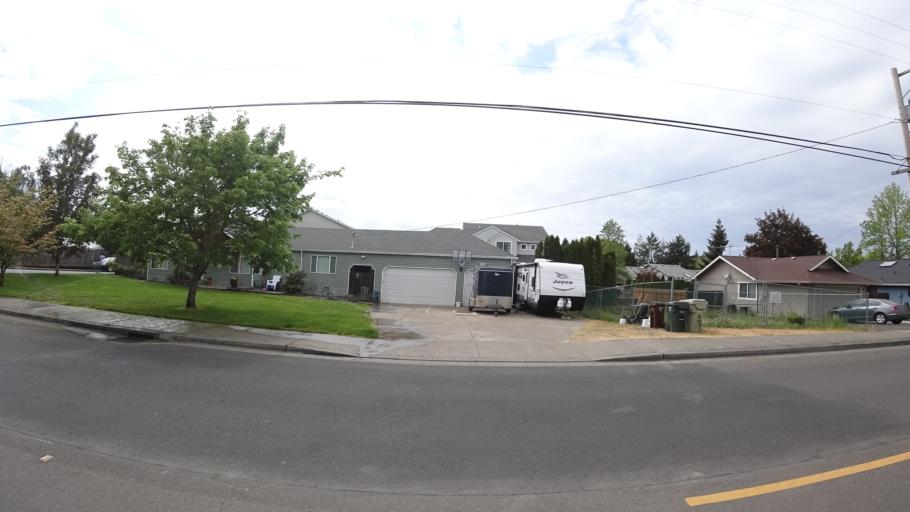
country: US
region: Oregon
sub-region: Washington County
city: Aloha
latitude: 45.5068
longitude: -122.9226
